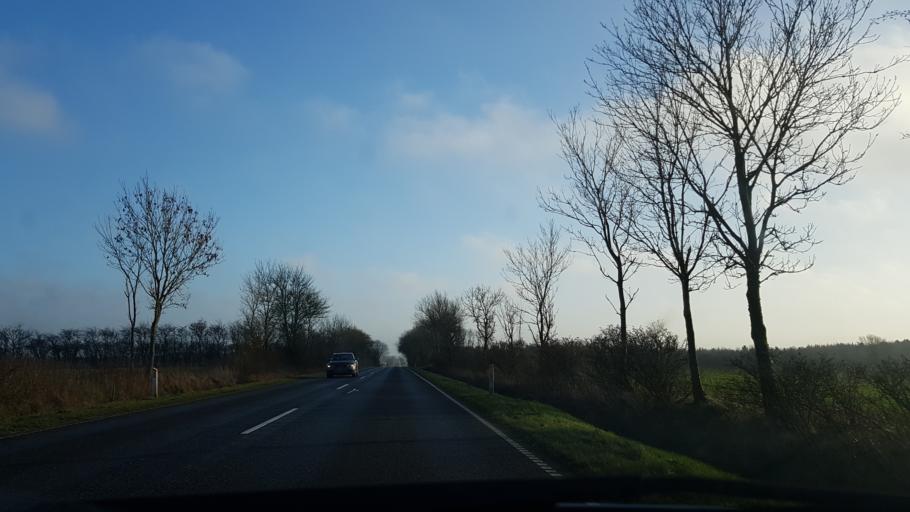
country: DK
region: South Denmark
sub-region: Haderslev Kommune
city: Vojens
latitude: 55.1792
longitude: 9.2382
